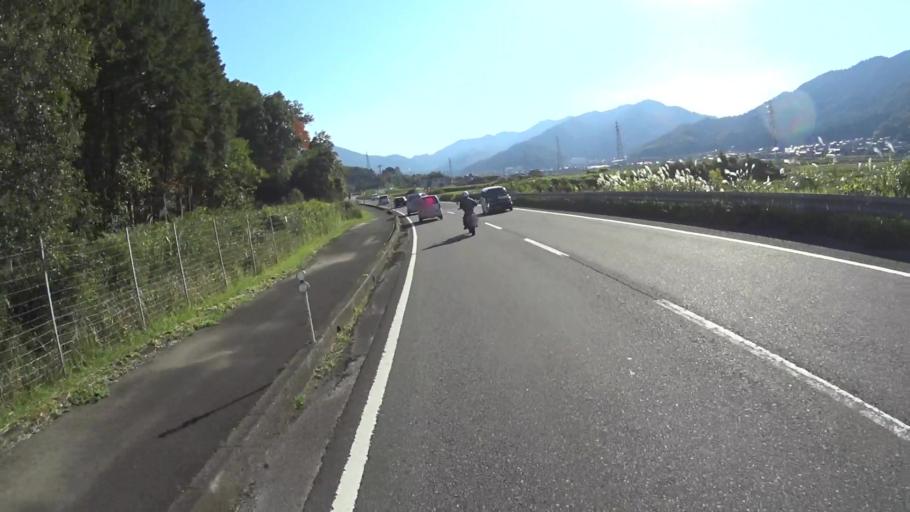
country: JP
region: Kyoto
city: Miyazu
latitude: 35.4934
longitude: 135.1005
